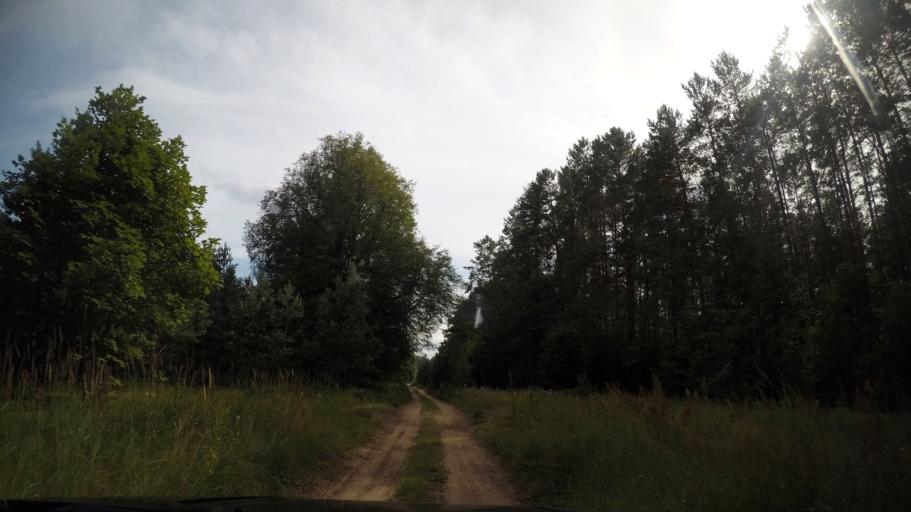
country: BY
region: Grodnenskaya
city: Skidal'
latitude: 53.8249
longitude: 24.1787
